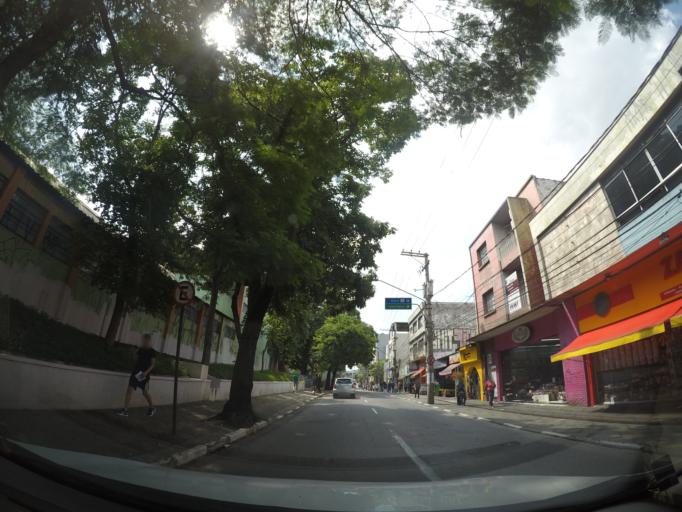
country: BR
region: Sao Paulo
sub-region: Guarulhos
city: Guarulhos
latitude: -23.4672
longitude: -46.5286
